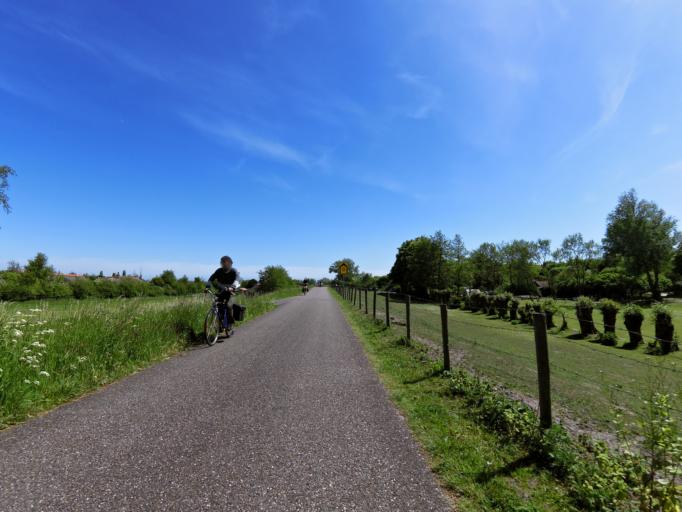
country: NL
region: South Holland
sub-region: Gemeente Hellevoetsluis
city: Nieuw-Helvoet
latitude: 51.8321
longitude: 4.0928
